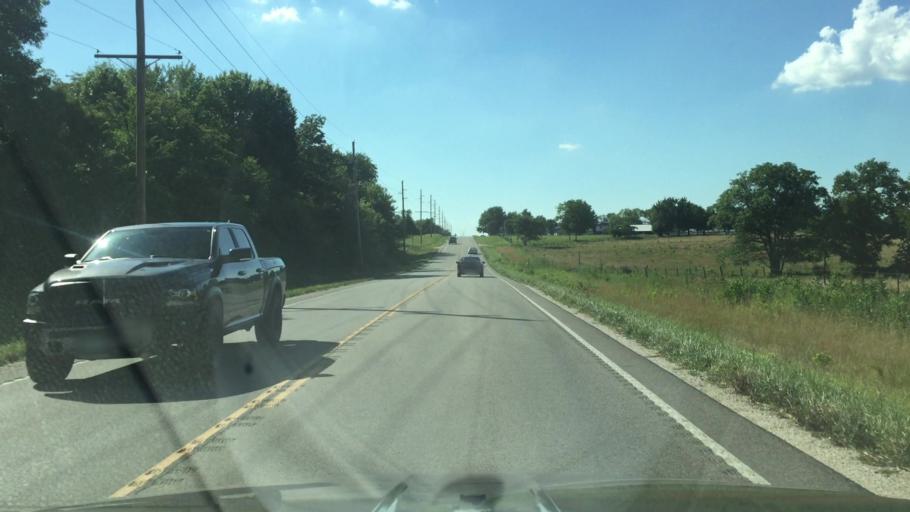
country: US
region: Missouri
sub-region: Morgan County
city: Versailles
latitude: 38.4428
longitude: -92.7893
